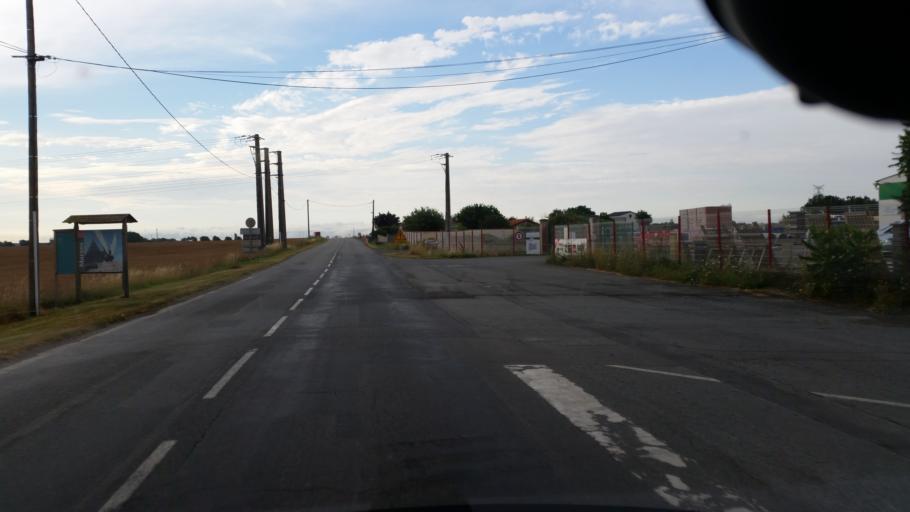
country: FR
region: Poitou-Charentes
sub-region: Departement de la Charente-Maritime
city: Marans
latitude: 46.3018
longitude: -0.9830
